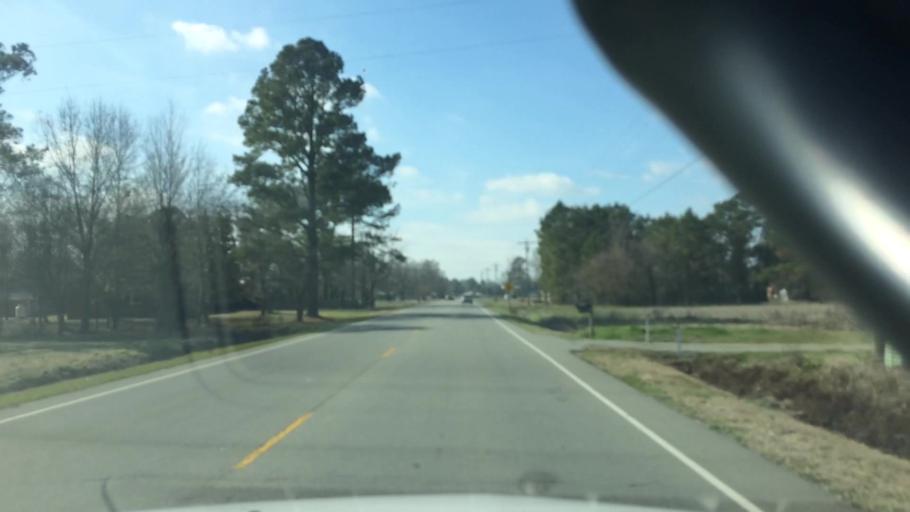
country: US
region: North Carolina
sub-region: Duplin County
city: Wallace
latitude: 34.7860
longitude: -77.8998
